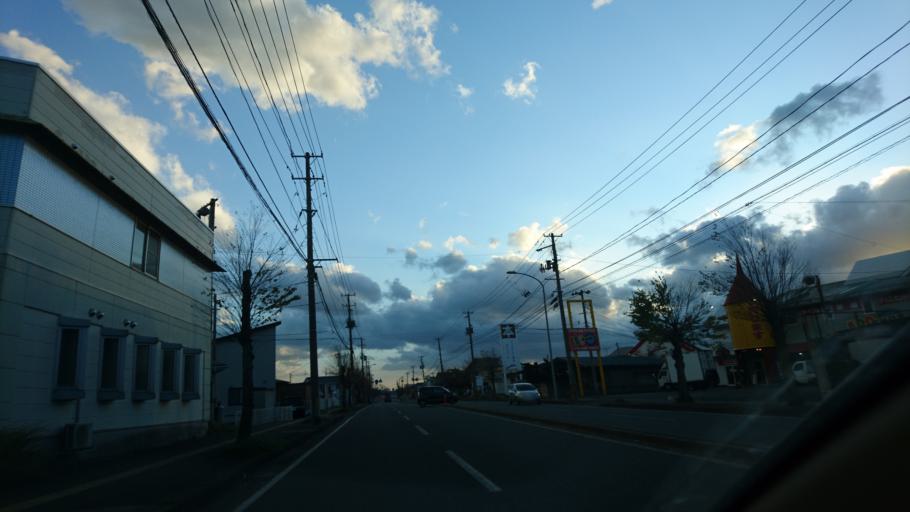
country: JP
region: Iwate
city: Mizusawa
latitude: 39.1510
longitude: 141.1328
